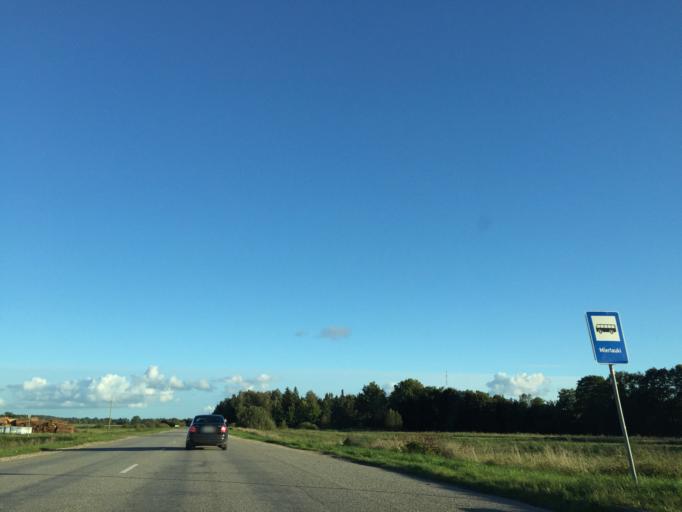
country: LV
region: Kuldigas Rajons
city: Kuldiga
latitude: 56.9558
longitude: 22.0070
